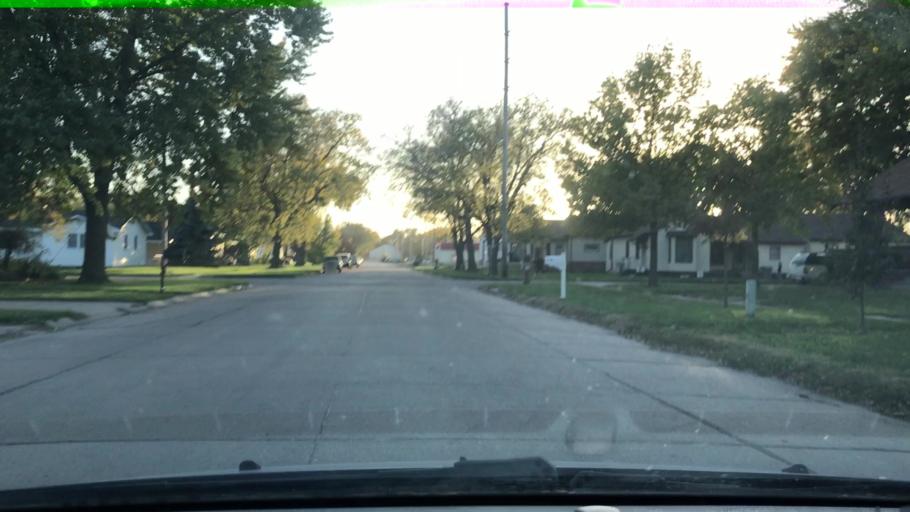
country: US
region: Nebraska
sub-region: Merrick County
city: Central City
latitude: 41.1125
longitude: -98.0060
